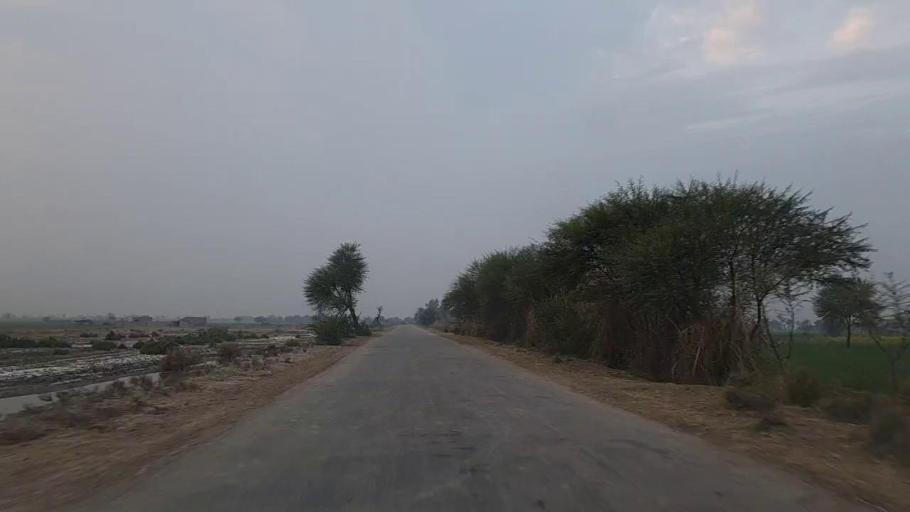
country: PK
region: Sindh
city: Jam Sahib
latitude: 26.3200
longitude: 68.5570
